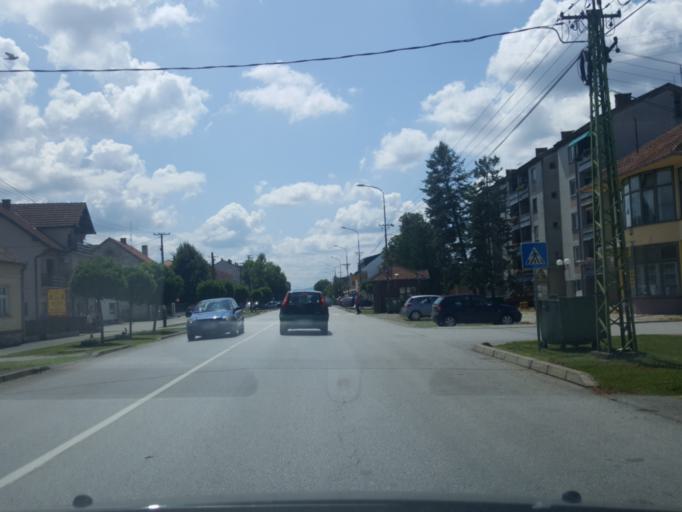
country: RS
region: Central Serbia
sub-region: Macvanski Okrug
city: Bogatic
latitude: 44.8382
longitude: 19.4804
